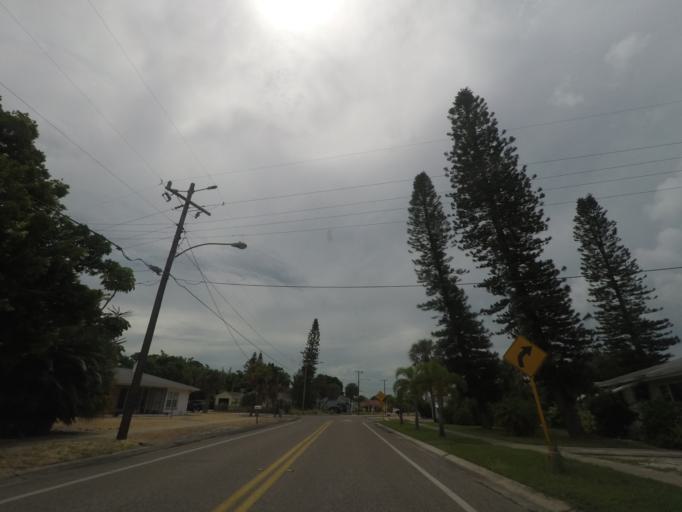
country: US
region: Florida
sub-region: Pinellas County
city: South Pasadena
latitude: 27.7451
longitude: -82.7539
